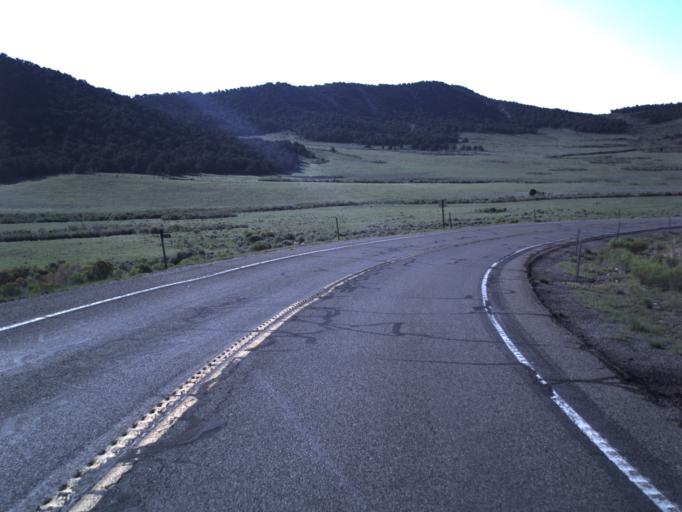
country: US
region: Utah
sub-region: Wayne County
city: Loa
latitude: 38.6875
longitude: -111.3987
